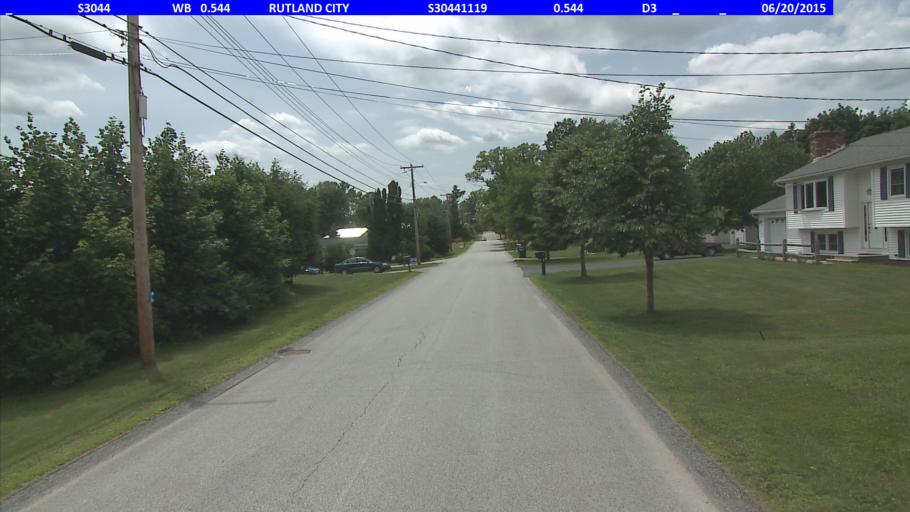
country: US
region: Vermont
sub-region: Rutland County
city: Rutland
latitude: 43.6205
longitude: -72.9635
